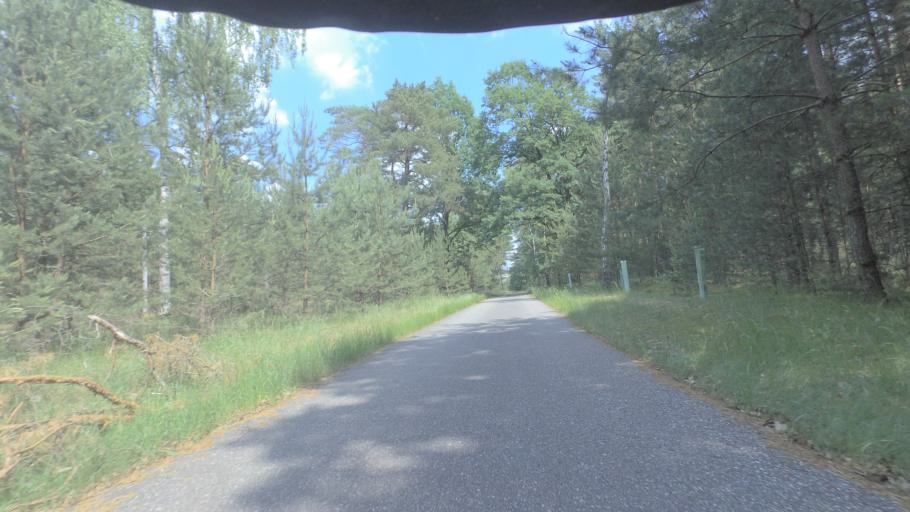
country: DE
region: Brandenburg
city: Fichtenwalde
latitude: 52.2525
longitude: 12.9066
